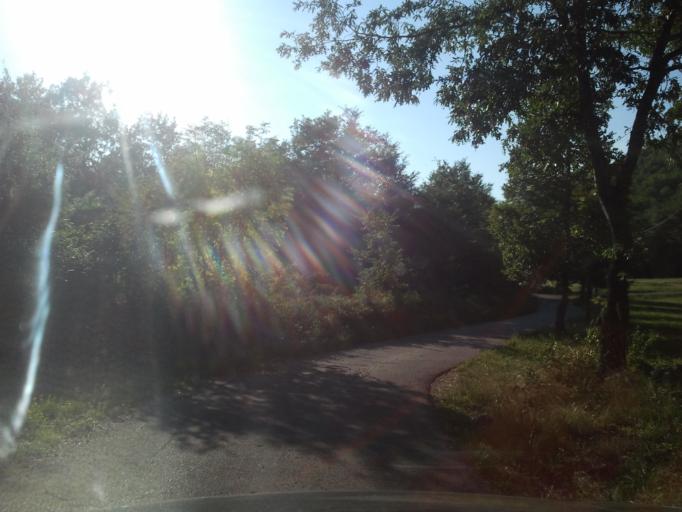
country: HR
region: Zadarska
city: Gracac
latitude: 44.3625
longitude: 15.7130
